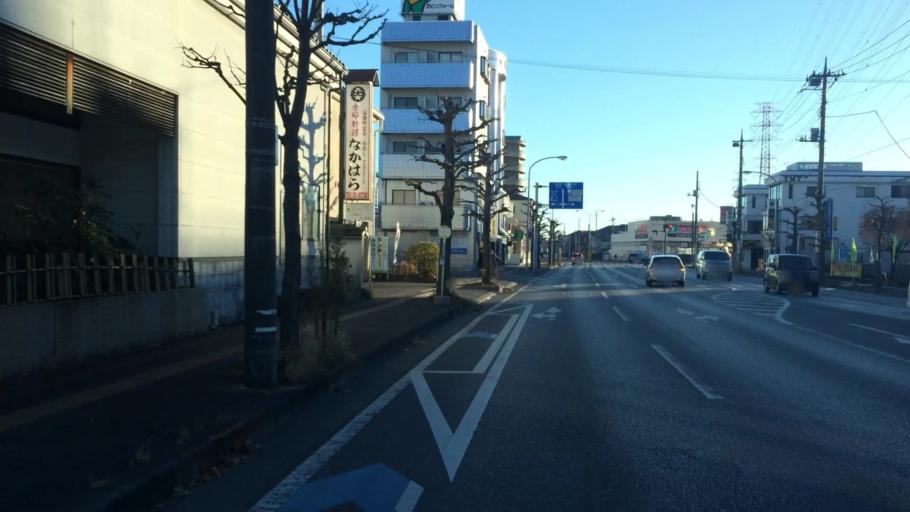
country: JP
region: Tochigi
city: Utsunomiya-shi
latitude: 36.5544
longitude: 139.9031
